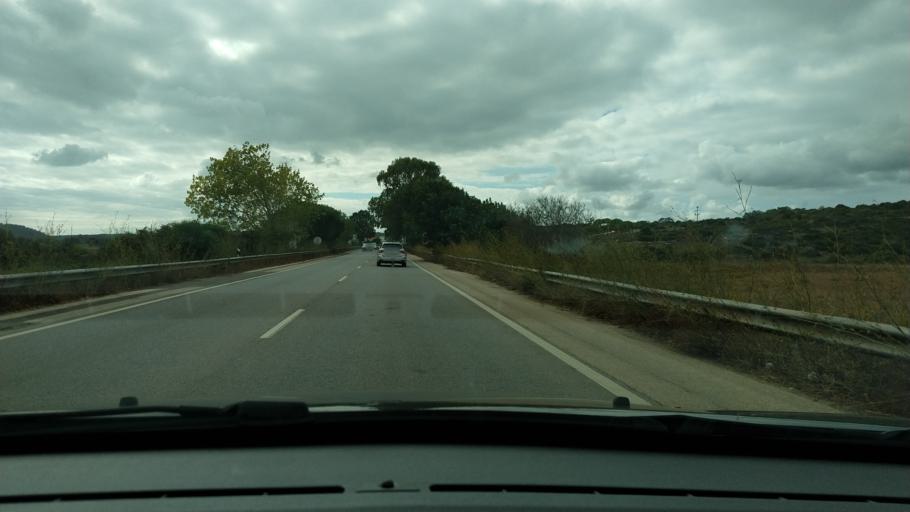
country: PT
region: Faro
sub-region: Lagos
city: Lagos
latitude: 37.0920
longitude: -8.7776
